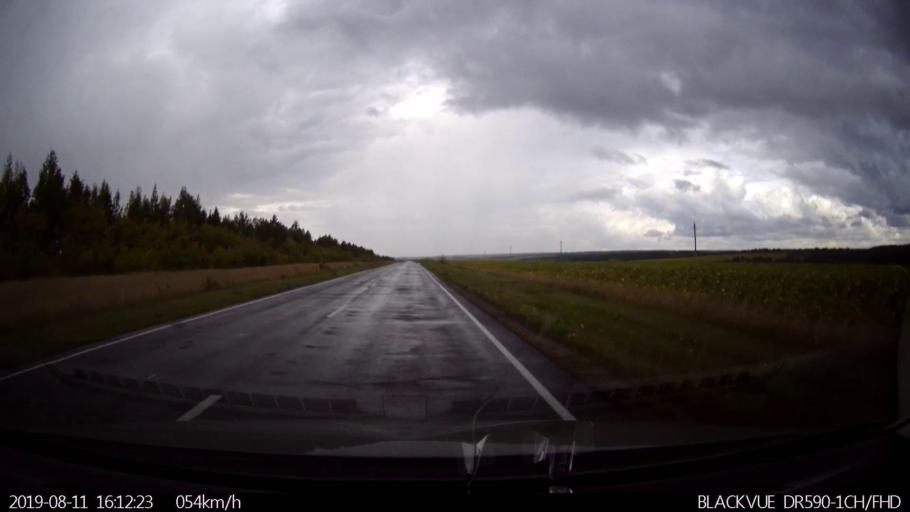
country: RU
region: Ulyanovsk
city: Ignatovka
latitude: 54.0110
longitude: 47.6406
